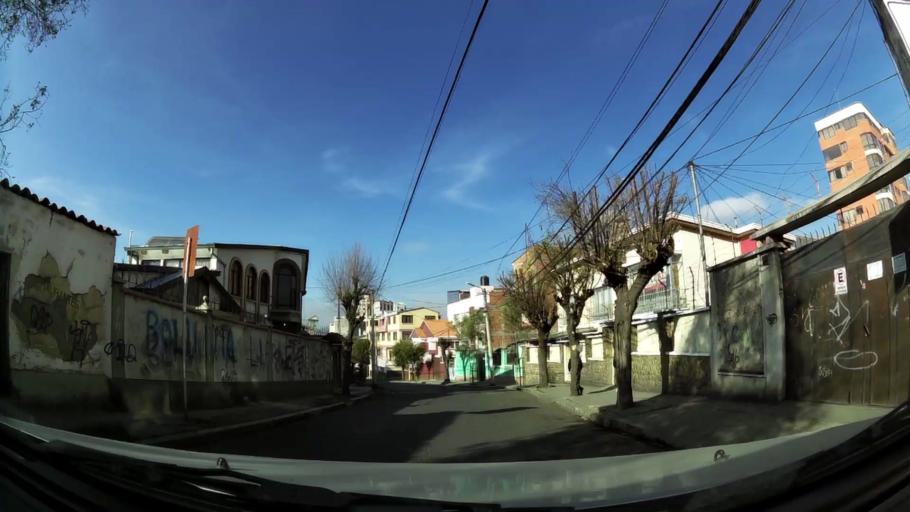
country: BO
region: La Paz
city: La Paz
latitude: -16.4934
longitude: -68.1204
